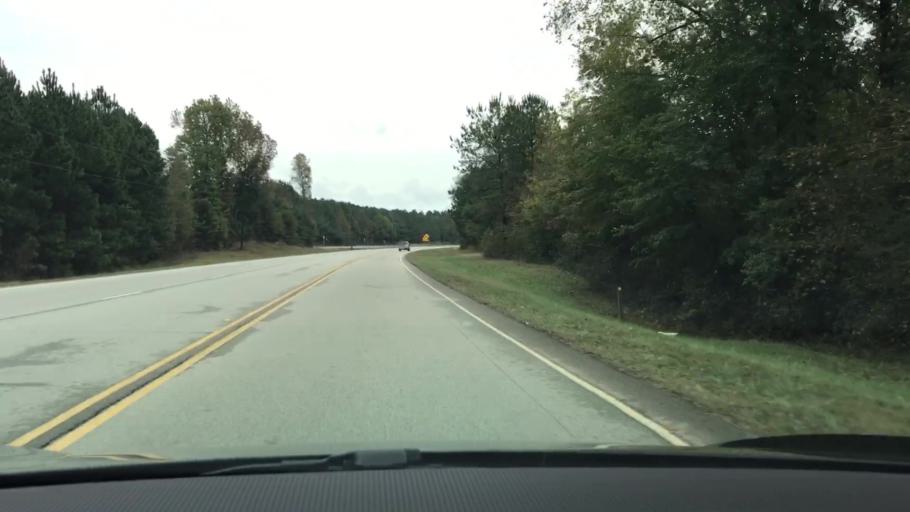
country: US
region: Georgia
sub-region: Warren County
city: Firing Range
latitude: 33.4787
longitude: -82.7380
